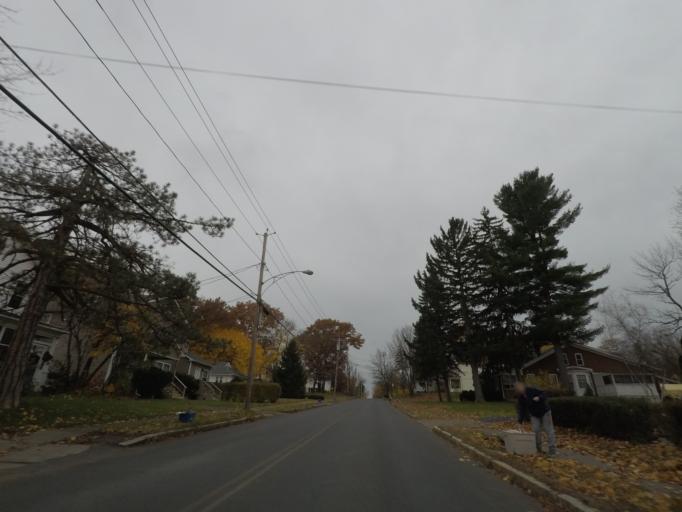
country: US
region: New York
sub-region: Albany County
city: Cohoes
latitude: 42.7865
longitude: -73.7170
